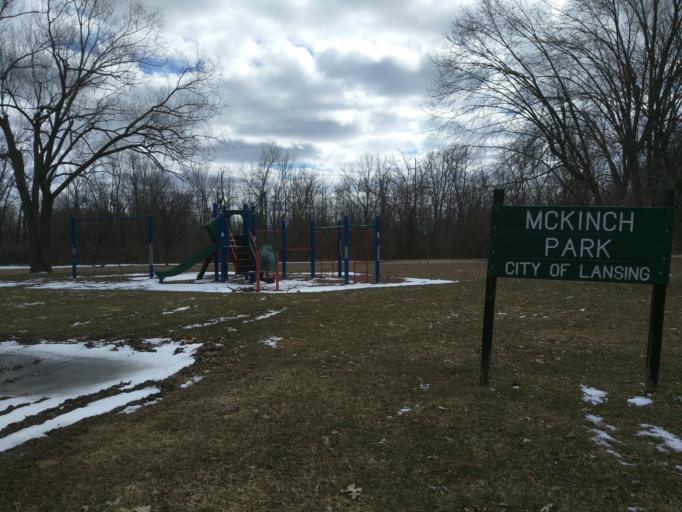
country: US
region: Michigan
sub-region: Ingham County
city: Lansing
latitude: 42.6794
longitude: -84.5772
